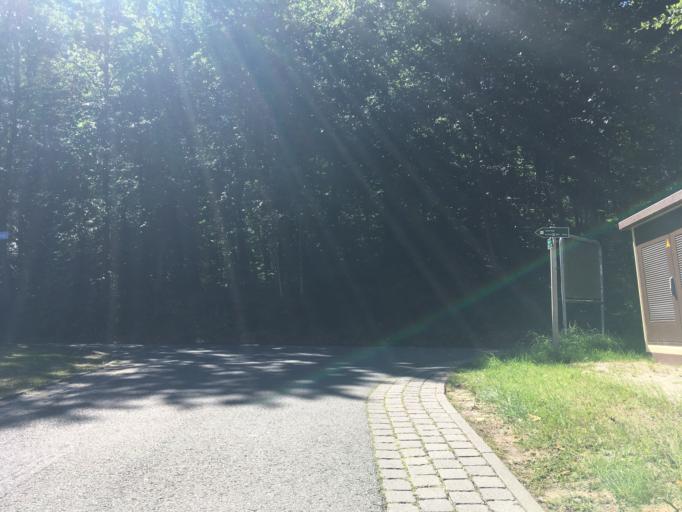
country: DE
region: Brandenburg
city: Grosswoltersdorf
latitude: 53.1442
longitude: 13.0529
